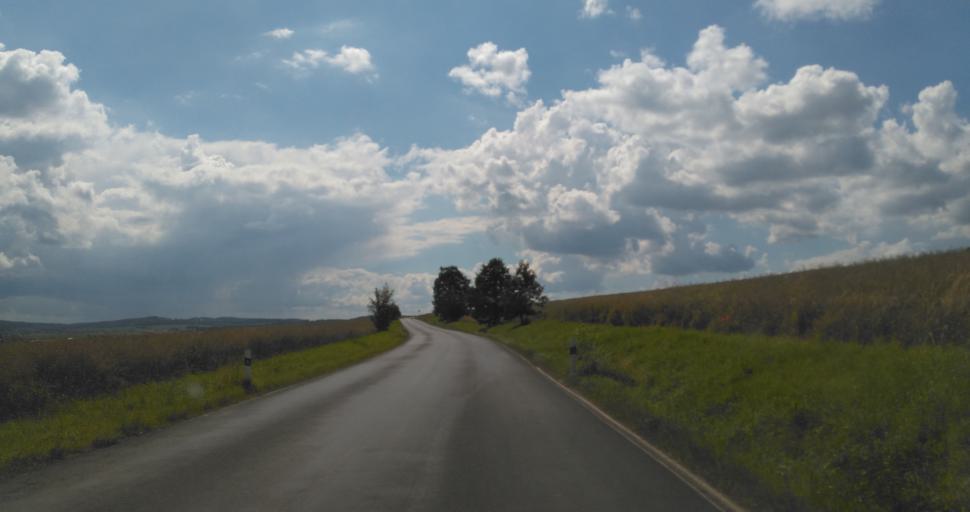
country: CZ
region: Central Bohemia
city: Lochovice
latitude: 49.8459
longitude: 13.9610
